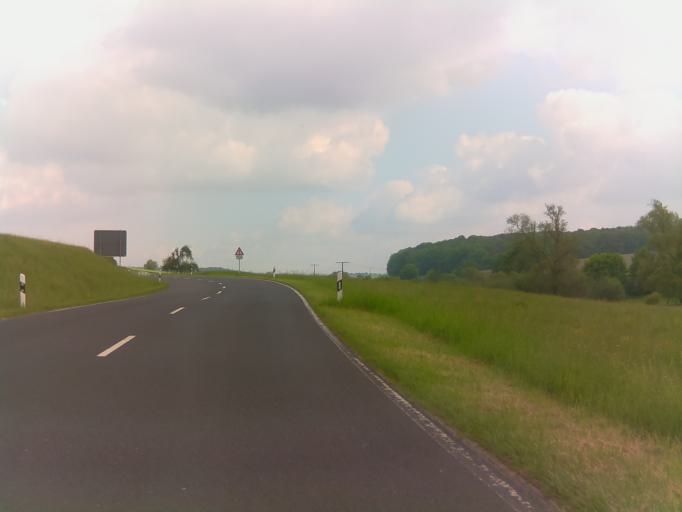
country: DE
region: Bavaria
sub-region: Regierungsbezirk Unterfranken
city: Wartmannsroth
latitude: 50.1470
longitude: 9.7785
